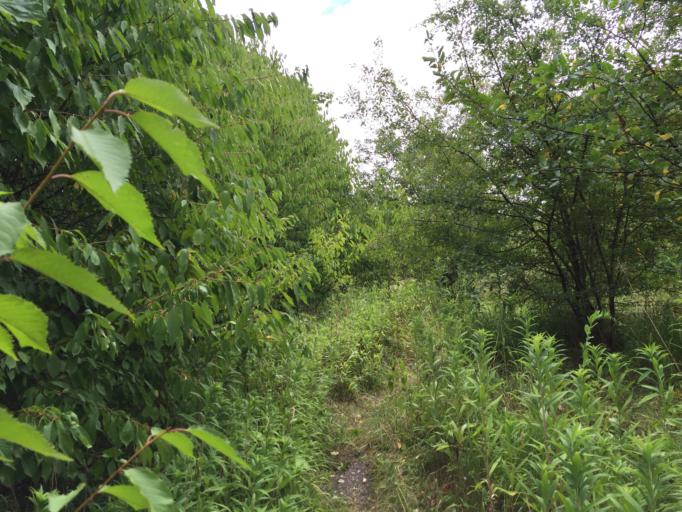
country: PL
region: Lesser Poland Voivodeship
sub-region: Krakow
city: Krakow
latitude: 50.0355
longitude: 19.9603
